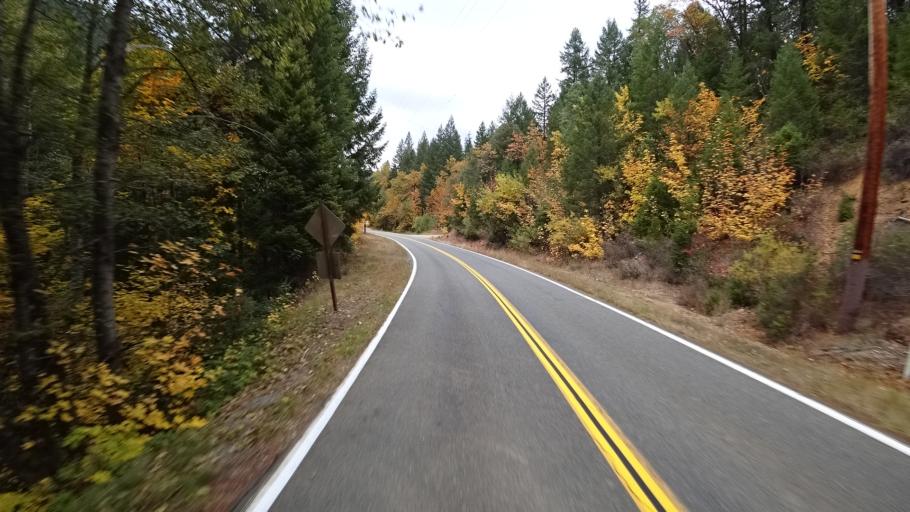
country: US
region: California
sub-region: Siskiyou County
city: Happy Camp
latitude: 41.8981
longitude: -123.4375
